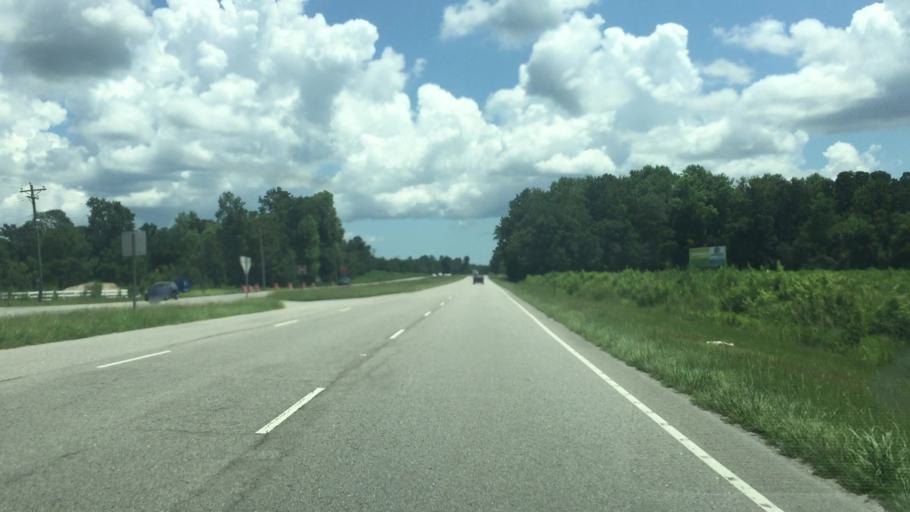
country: US
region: South Carolina
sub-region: Horry County
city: Loris
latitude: 34.0060
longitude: -78.7619
